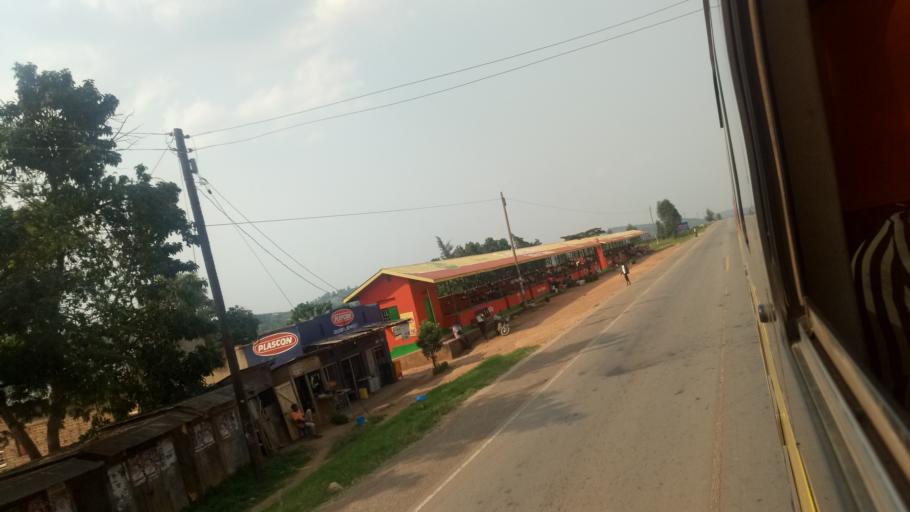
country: UG
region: Western Region
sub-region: Mbarara District
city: Mbarara
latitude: -0.5307
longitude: 30.7196
